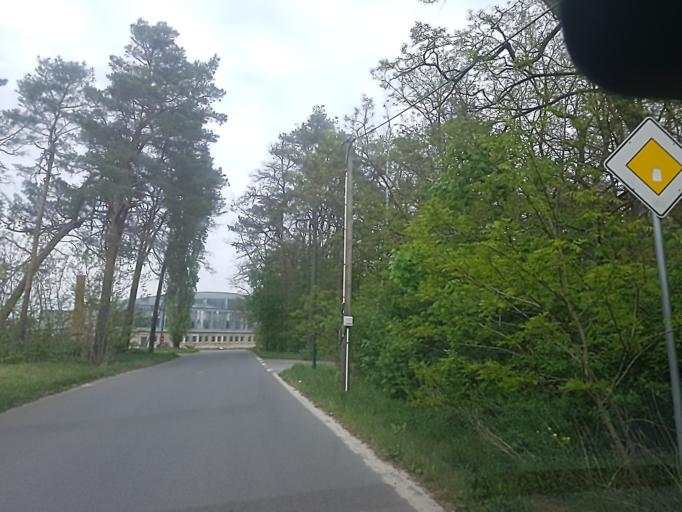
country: DE
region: Brandenburg
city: Finsterwalde
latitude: 51.6006
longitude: 13.7406
